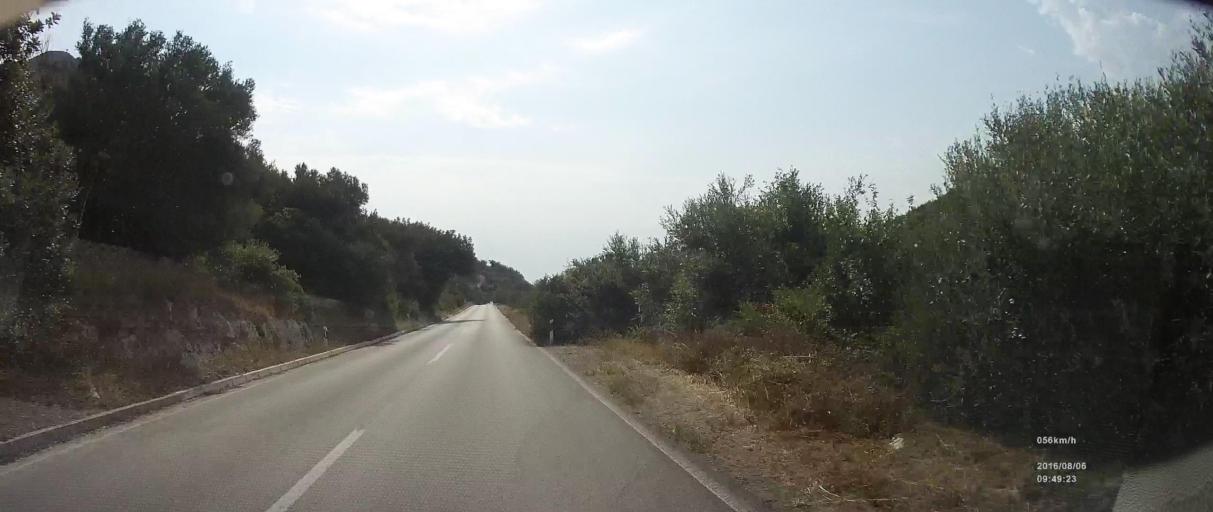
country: HR
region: Dubrovacko-Neretvanska
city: Blato
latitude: 42.7376
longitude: 17.5410
